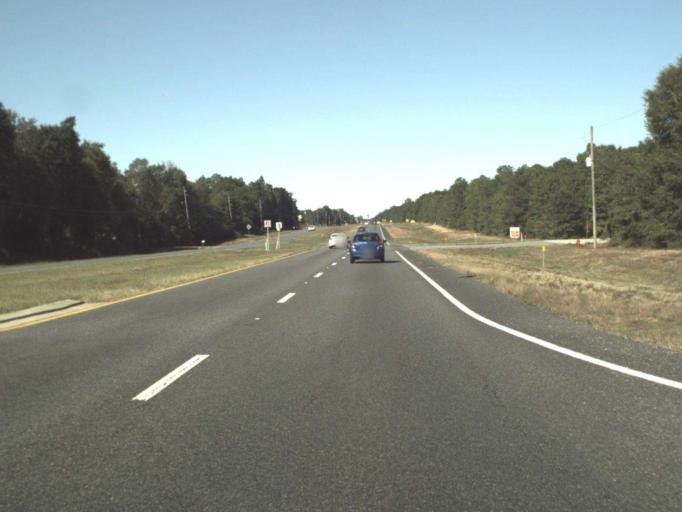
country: US
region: Florida
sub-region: Santa Rosa County
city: East Milton
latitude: 30.6018
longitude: -86.9472
